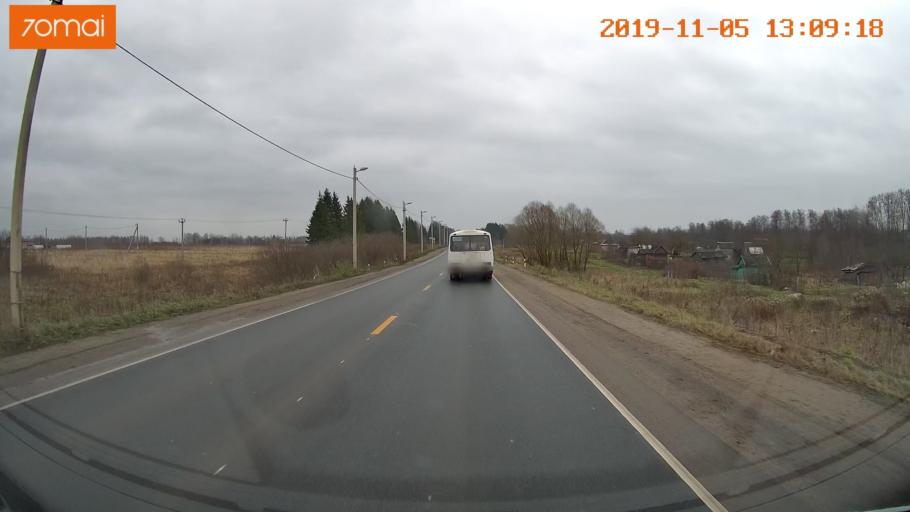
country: RU
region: Ivanovo
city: Kitovo
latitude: 56.8631
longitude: 41.3038
